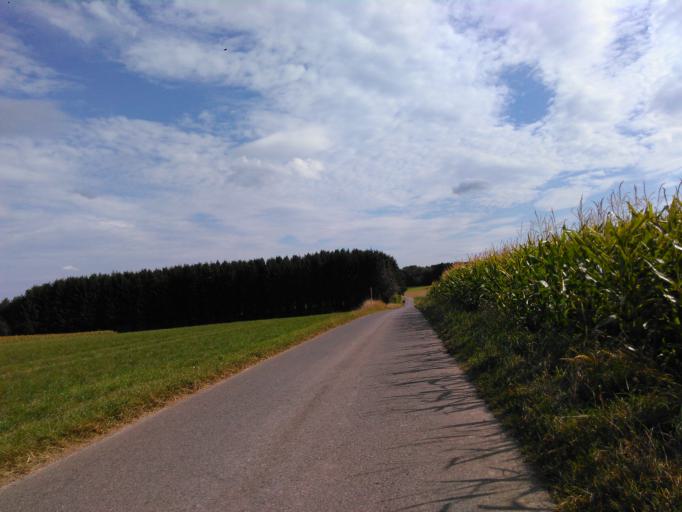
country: BE
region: Wallonia
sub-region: Province du Luxembourg
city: Gouvy
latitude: 50.1665
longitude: 5.9656
